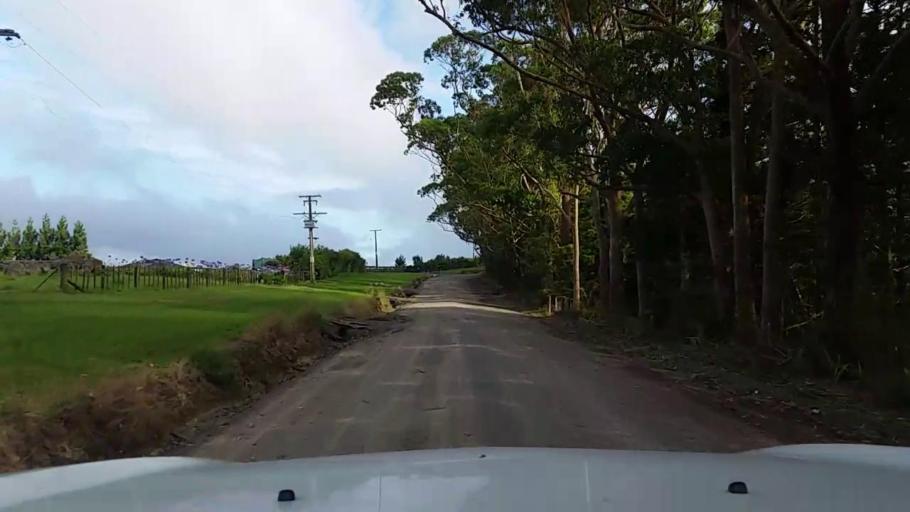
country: NZ
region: Northland
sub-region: Whangarei
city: Maungatapere
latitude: -35.6720
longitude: 174.1752
